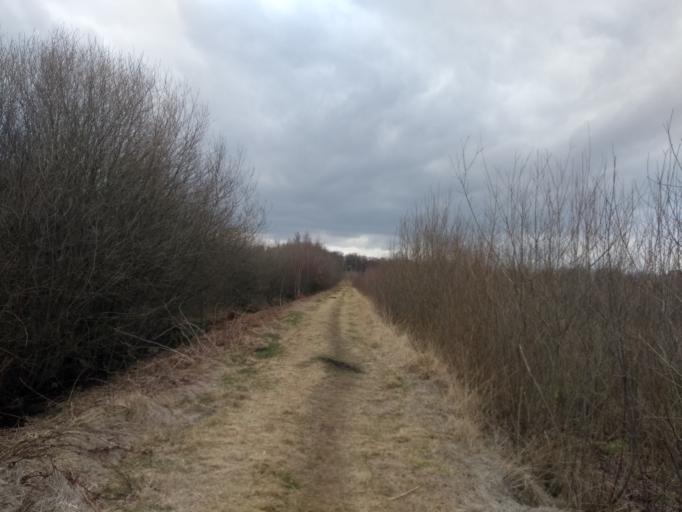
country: NL
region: Overijssel
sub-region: Gemeente Haaksbergen
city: Haaksbergen
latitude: 52.1205
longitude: 6.7731
